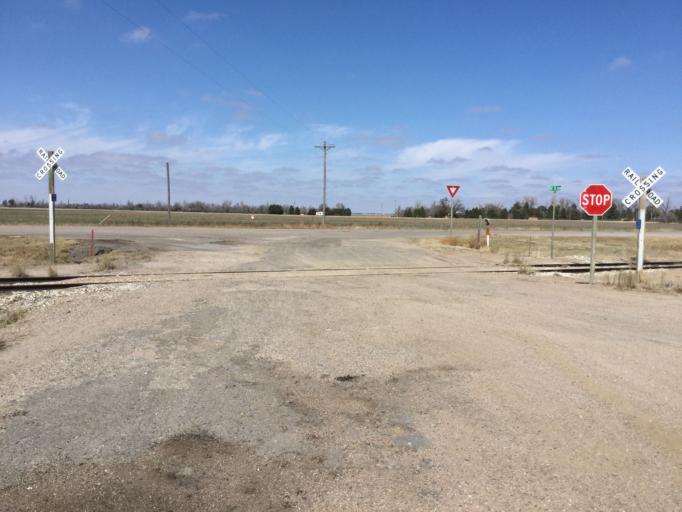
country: US
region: Kansas
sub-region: Barton County
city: Great Bend
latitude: 38.3137
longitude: -98.8779
